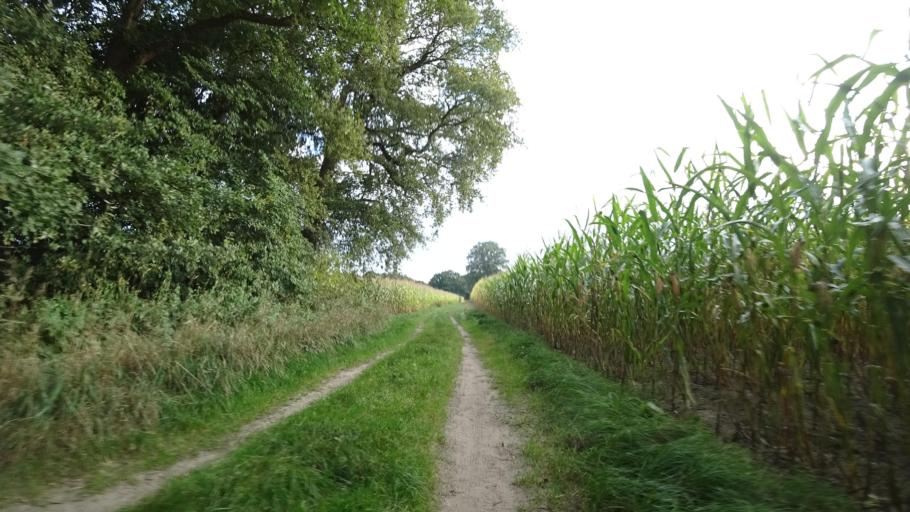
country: DE
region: North Rhine-Westphalia
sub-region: Regierungsbezirk Detmold
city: Rheda-Wiedenbruck
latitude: 51.9003
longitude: 8.3224
